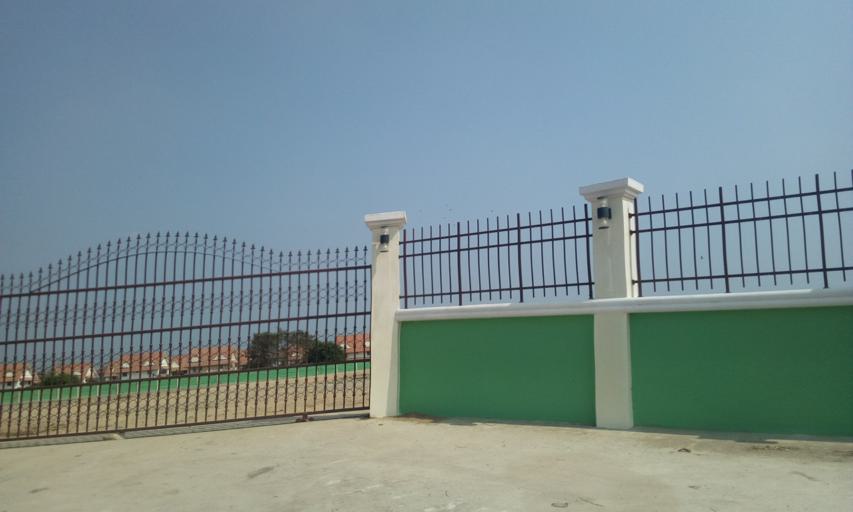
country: TH
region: Pathum Thani
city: Ban Rangsit
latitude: 14.0243
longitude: 100.7593
